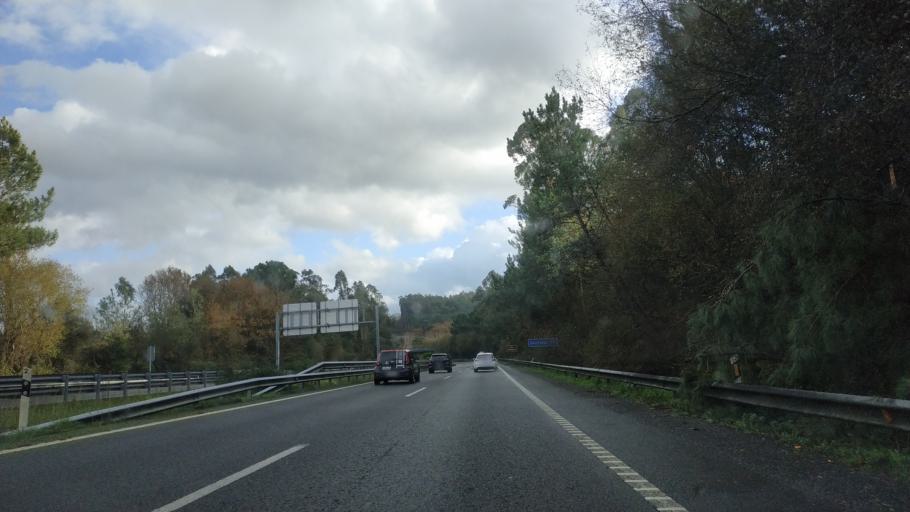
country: ES
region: Galicia
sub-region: Provincia da Coruna
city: Culleredo
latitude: 43.2701
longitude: -8.3931
